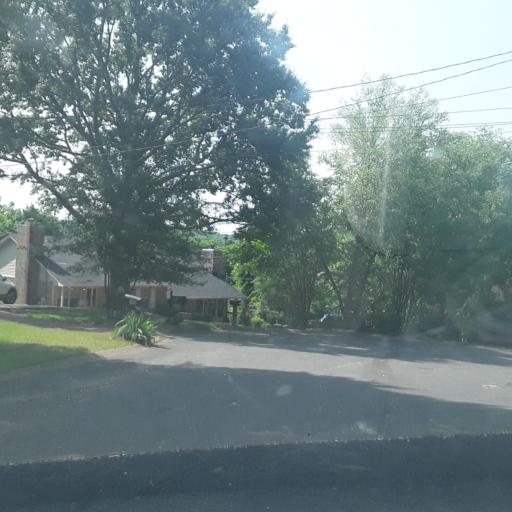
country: US
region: Tennessee
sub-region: Williamson County
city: Brentwood
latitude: 36.0457
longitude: -86.7473
